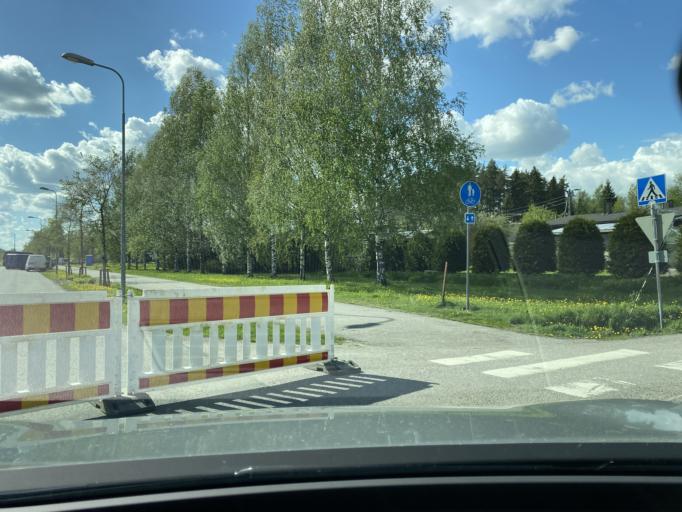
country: FI
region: Uusimaa
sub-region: Helsinki
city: Maentsaelae
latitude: 60.6457
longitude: 25.3233
